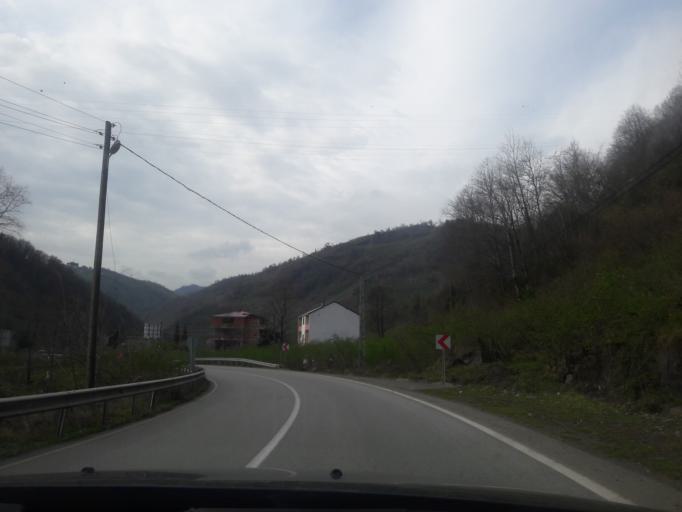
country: TR
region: Trabzon
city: Besikduzu
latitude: 41.0459
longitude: 39.1965
